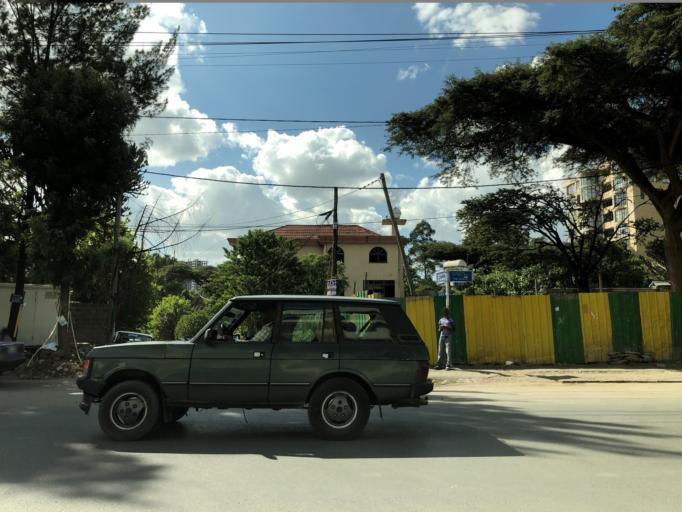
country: ET
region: Adis Abeba
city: Addis Ababa
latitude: 8.9988
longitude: 38.7793
